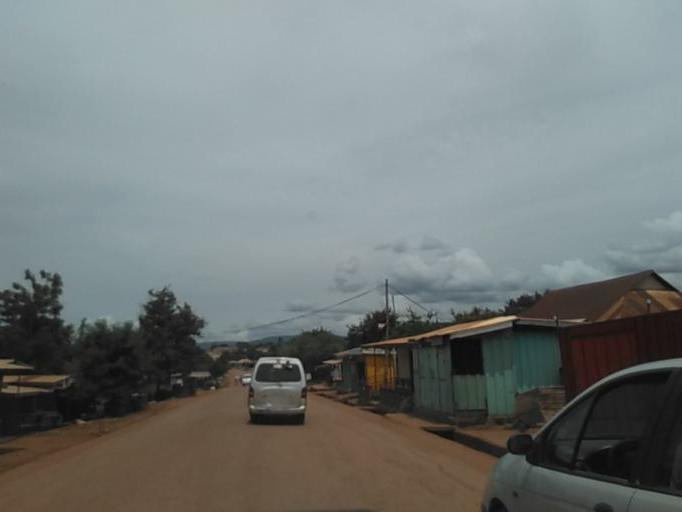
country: GH
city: Akropong
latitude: 6.1261
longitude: -0.0005
